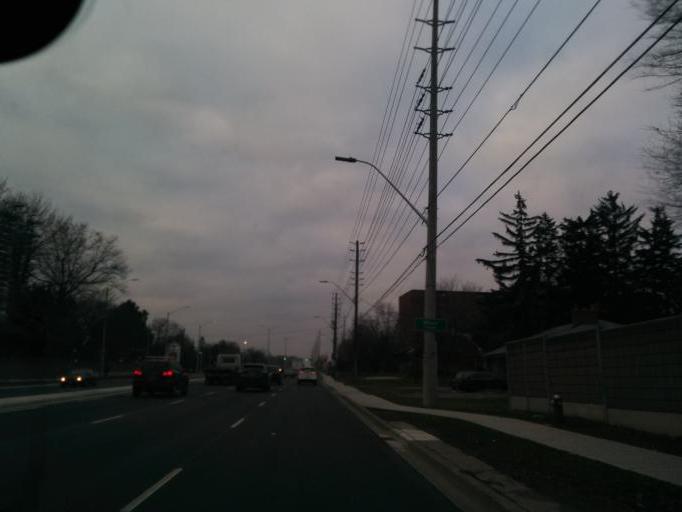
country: CA
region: Ontario
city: Etobicoke
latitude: 43.6155
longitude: -79.5925
